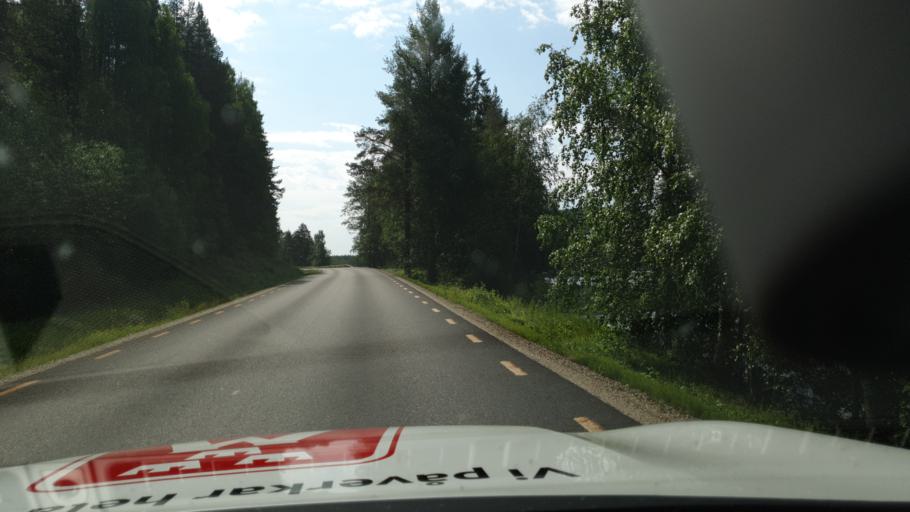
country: SE
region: Vaesterbotten
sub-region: Vindelns Kommun
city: Vindeln
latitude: 64.4449
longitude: 19.3392
